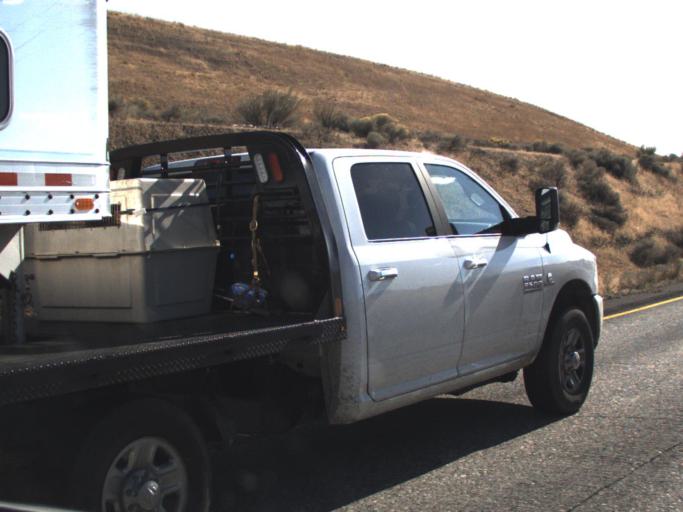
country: US
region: Oregon
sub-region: Umatilla County
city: Umatilla
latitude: 45.9755
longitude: -119.3346
